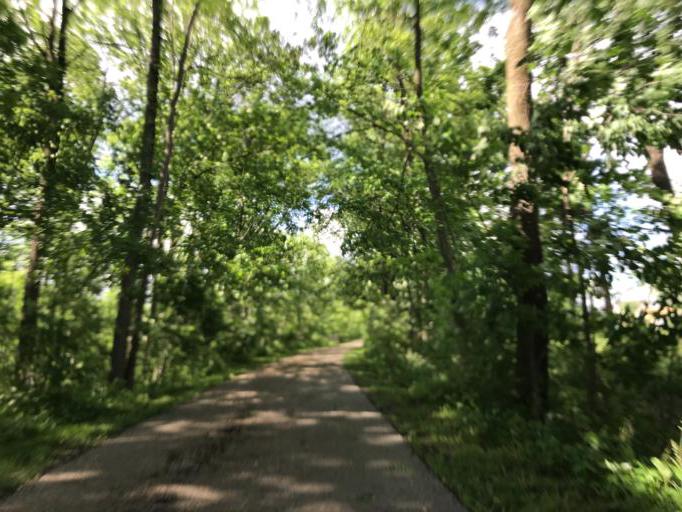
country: US
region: Michigan
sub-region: Oakland County
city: South Lyon
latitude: 42.4679
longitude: -83.6468
